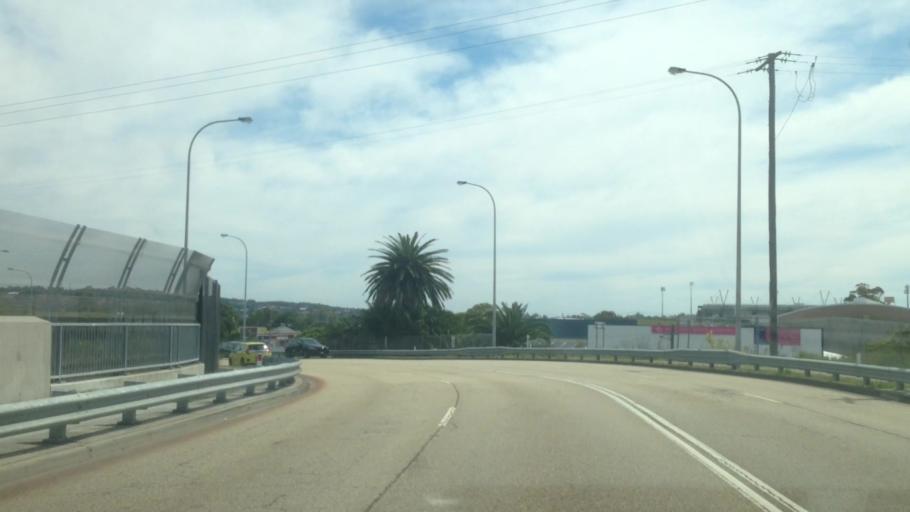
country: AU
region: New South Wales
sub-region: Newcastle
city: Broadmeadow
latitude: -32.9238
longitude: 151.7336
